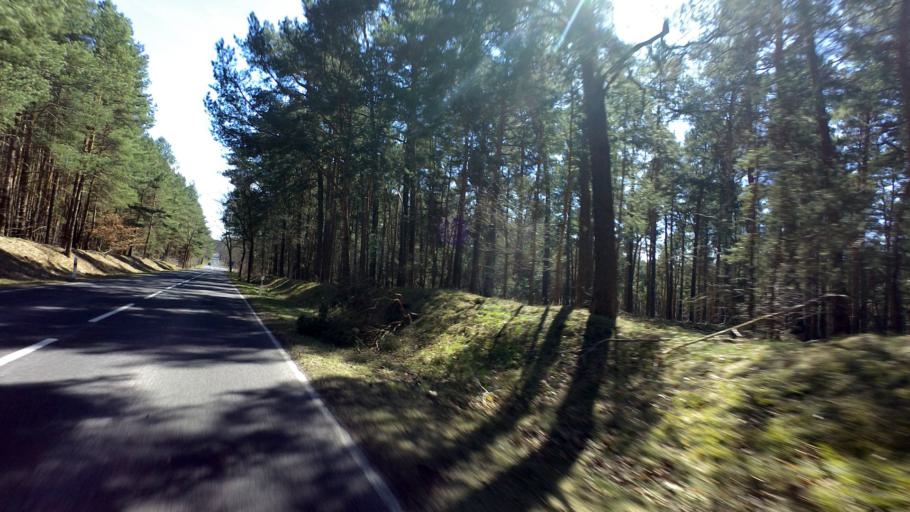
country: DE
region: Brandenburg
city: Teupitz
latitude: 52.1266
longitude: 13.6312
